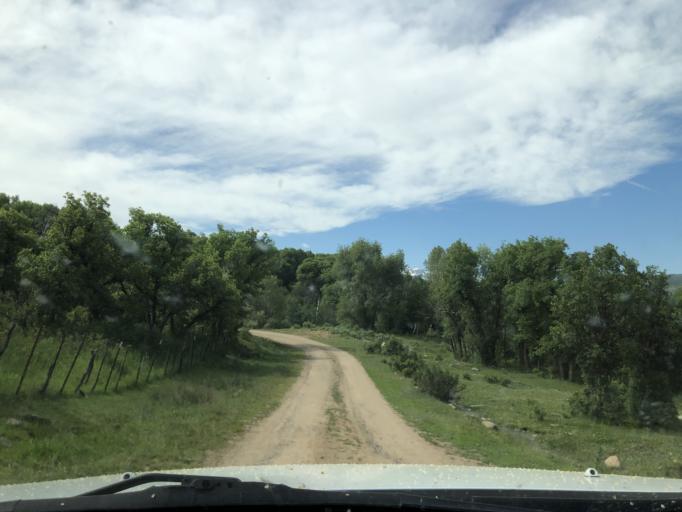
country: US
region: Colorado
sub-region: Delta County
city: Paonia
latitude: 39.0097
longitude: -107.3414
